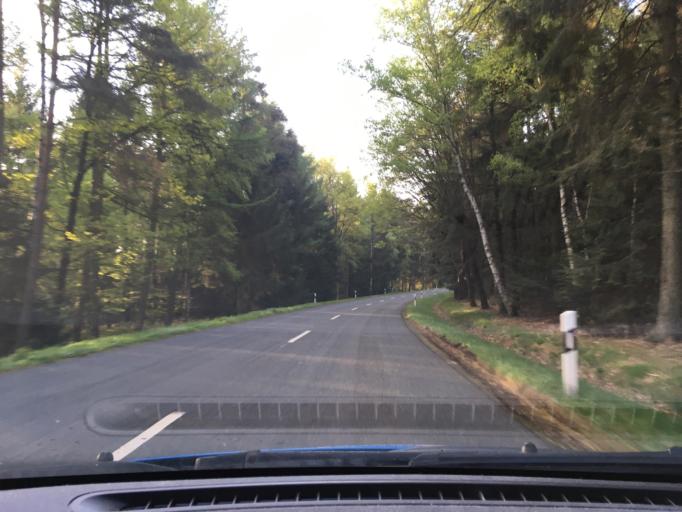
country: DE
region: Lower Saxony
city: Bispingen
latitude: 53.0039
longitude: 9.9969
